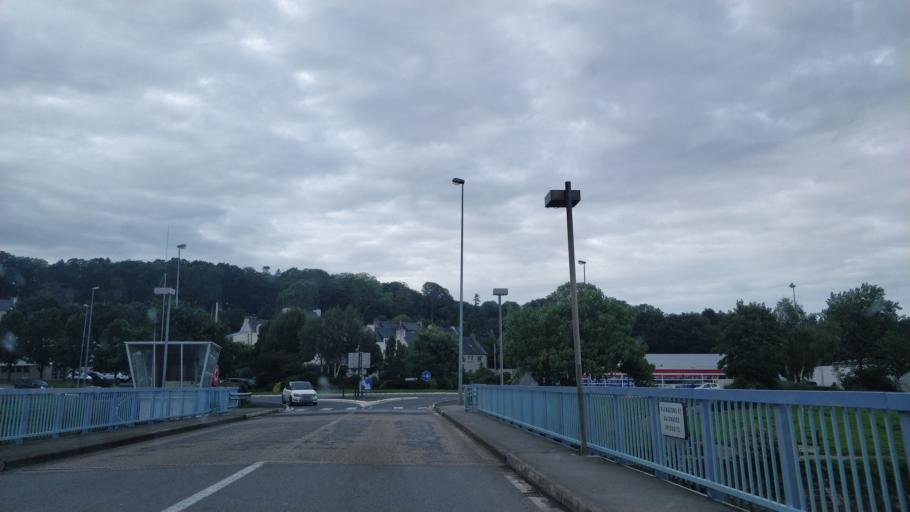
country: FR
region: Brittany
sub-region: Departement du Finistere
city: Landerneau
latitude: 48.4449
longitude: -4.2695
